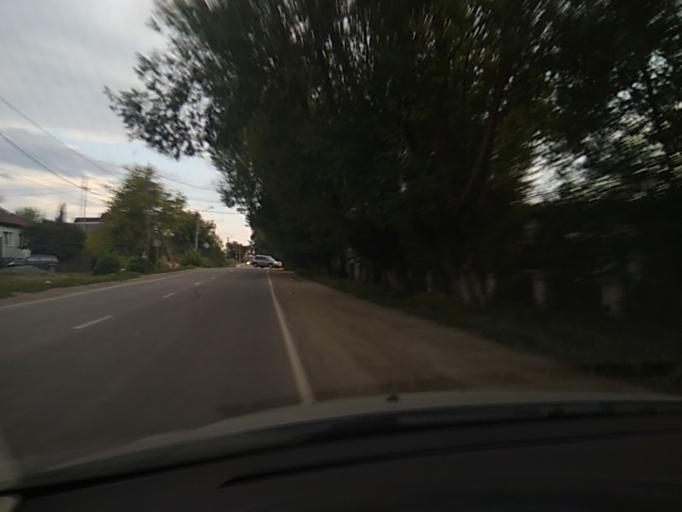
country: RU
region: Chelyabinsk
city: Kyshtym
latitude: 55.6992
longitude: 60.5526
